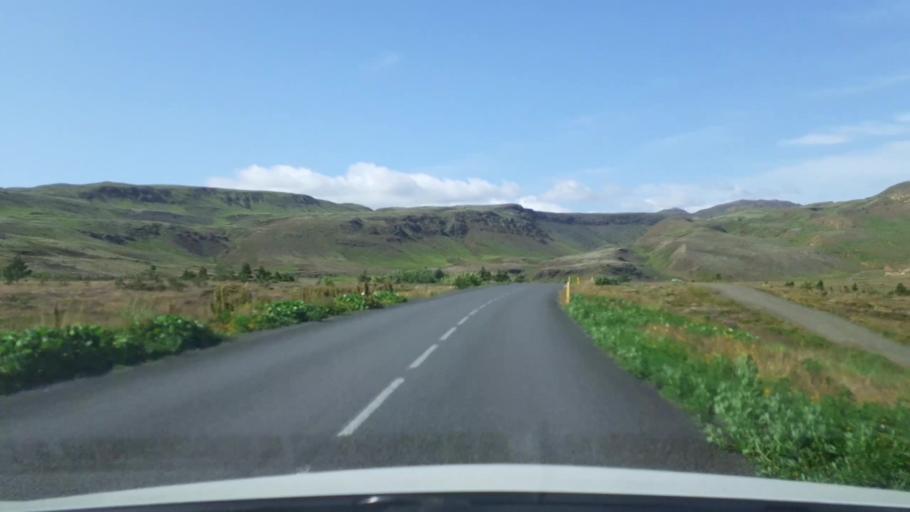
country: IS
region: South
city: Hveragerdi
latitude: 64.0151
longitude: -21.2097
